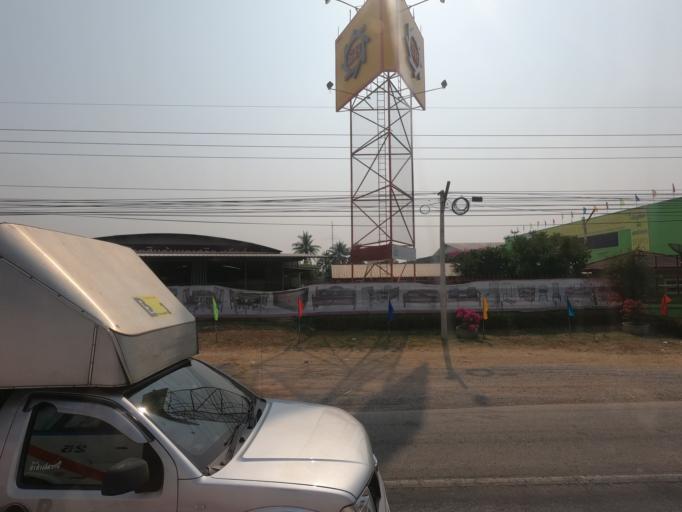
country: TH
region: Khon Kaen
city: Phon
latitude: 15.8823
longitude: 102.6401
